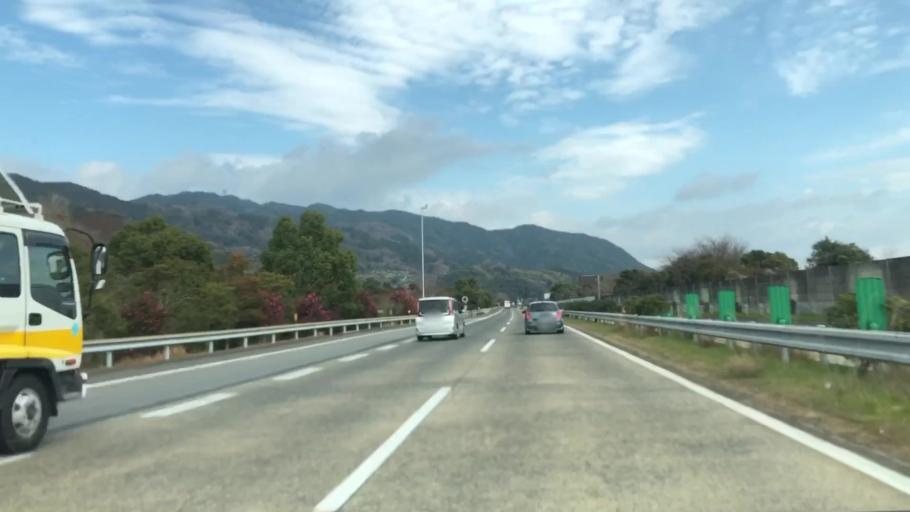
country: JP
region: Saga Prefecture
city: Saga-shi
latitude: 33.3235
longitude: 130.2813
